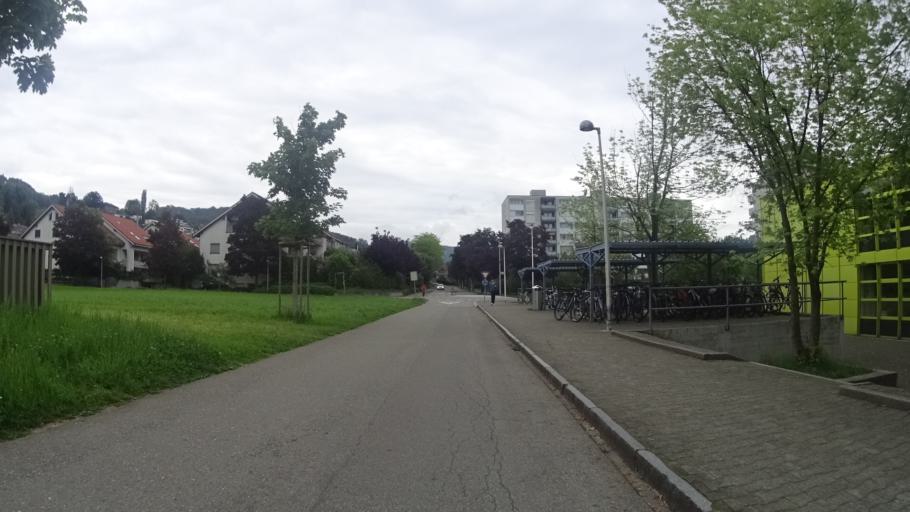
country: CH
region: Aargau
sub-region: Bezirk Baden
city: Obersiggenthal
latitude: 47.4913
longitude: 8.2856
